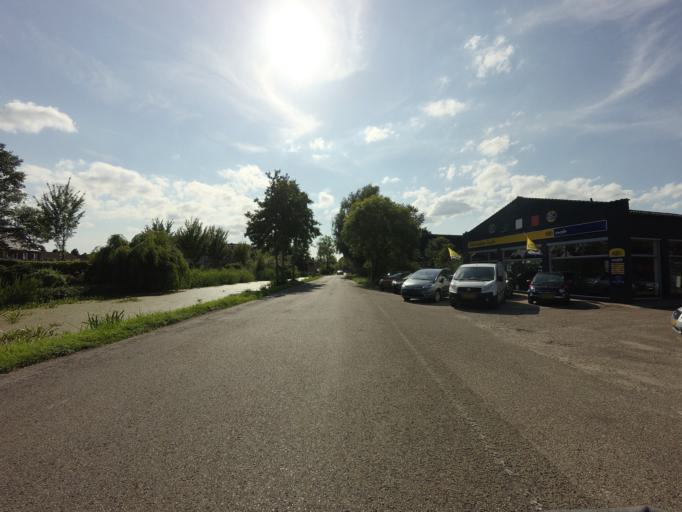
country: NL
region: Utrecht
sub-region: Gemeente Lopik
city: Lopik
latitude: 51.9756
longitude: 4.9526
